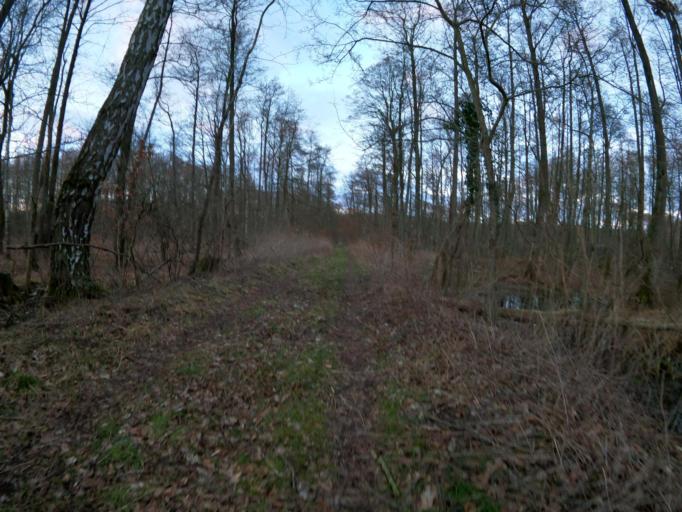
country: PL
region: West Pomeranian Voivodeship
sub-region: Powiat kamienski
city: Golczewo
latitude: 53.8320
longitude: 14.9543
